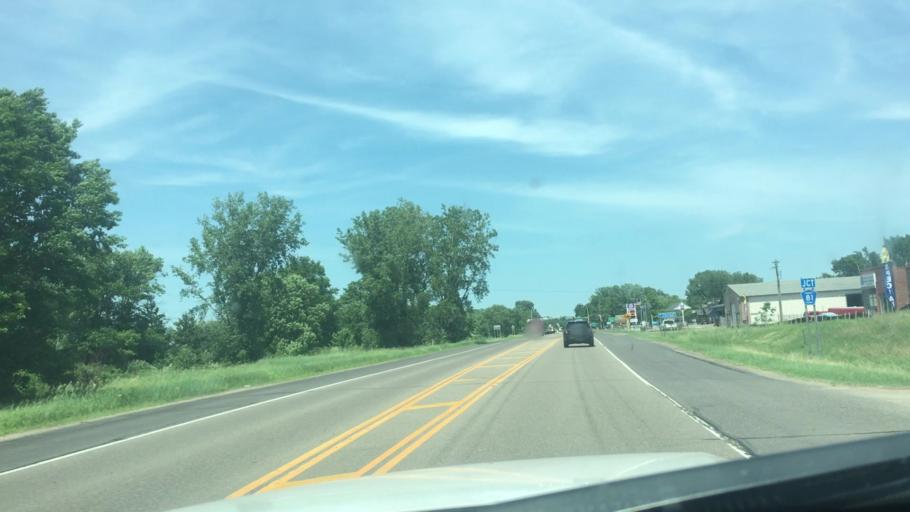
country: US
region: Minnesota
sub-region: Ramsey County
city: White Bear Lake
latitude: 45.1200
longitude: -93.0033
